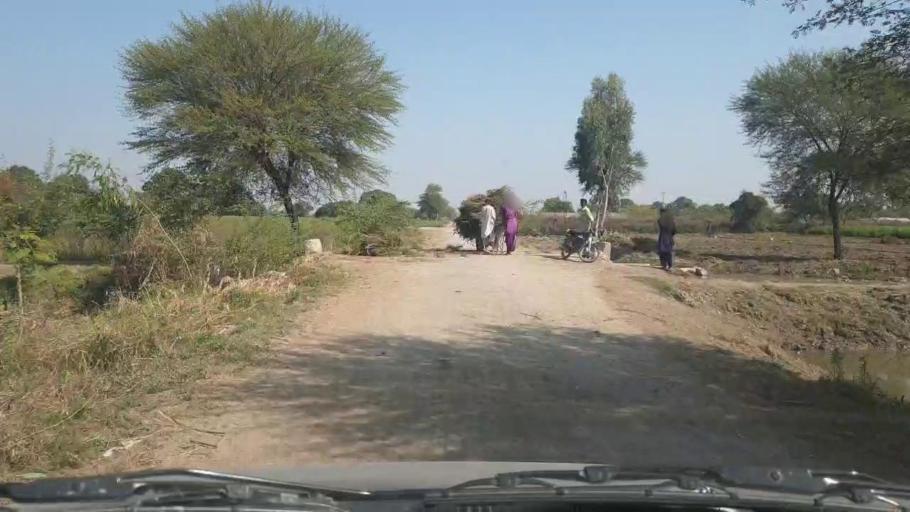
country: PK
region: Sindh
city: Samaro
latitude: 25.2987
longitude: 69.2927
